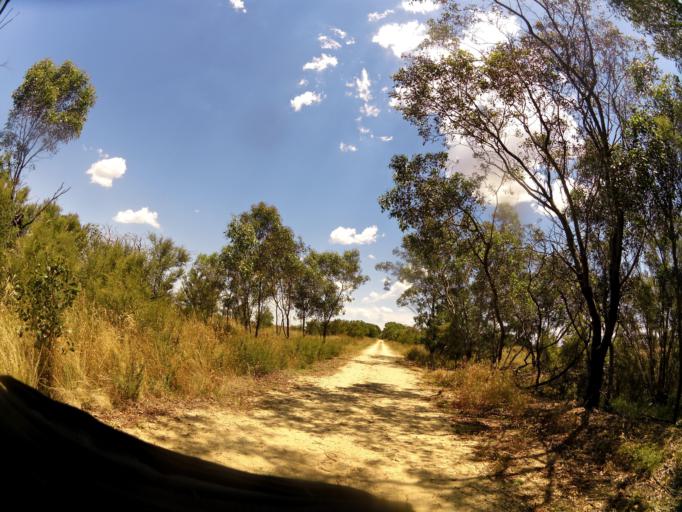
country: AU
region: Victoria
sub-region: Wellington
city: Heyfield
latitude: -37.9785
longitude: 146.8519
